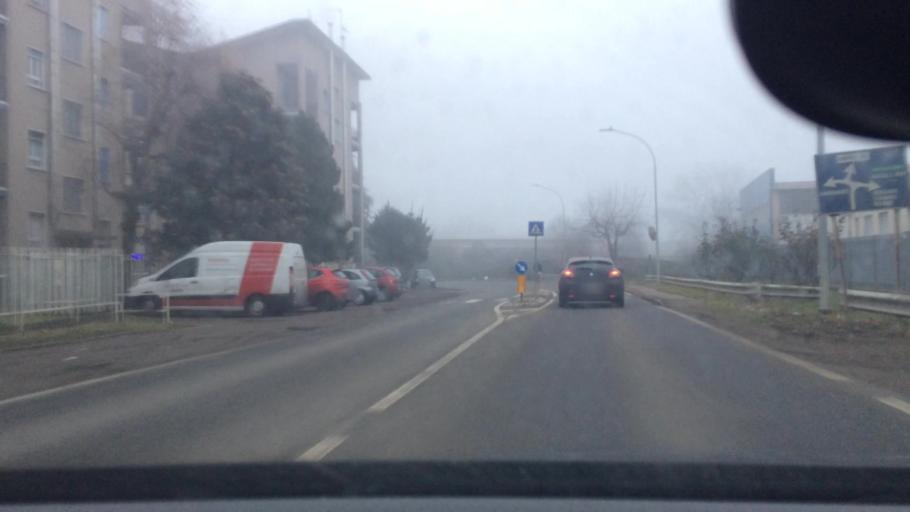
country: IT
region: Lombardy
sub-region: Citta metropolitana di Milano
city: Lainate
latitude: 45.5719
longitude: 9.0190
